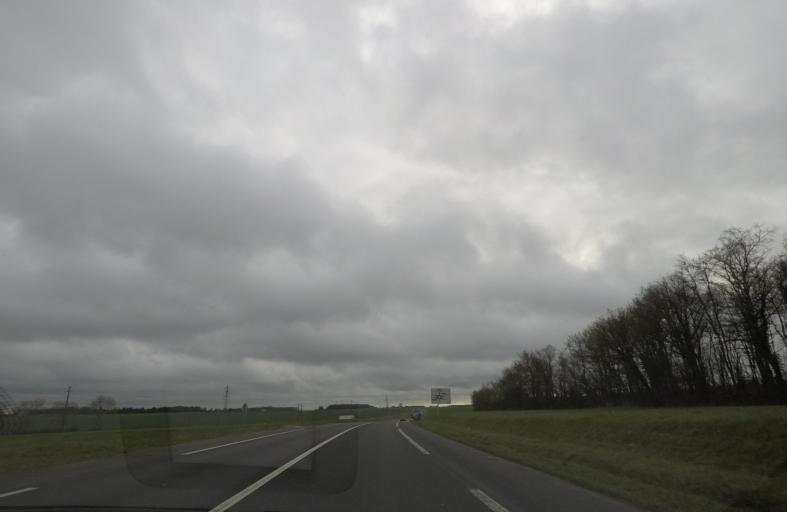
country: FR
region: Centre
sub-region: Departement du Loir-et-Cher
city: Vendome
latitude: 47.7738
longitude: 1.0566
